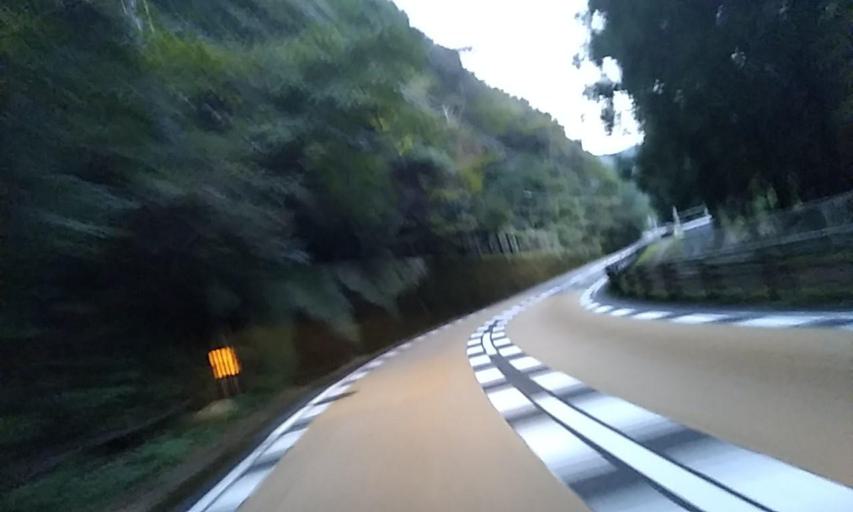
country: JP
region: Wakayama
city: Shingu
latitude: 33.7328
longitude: 135.9428
